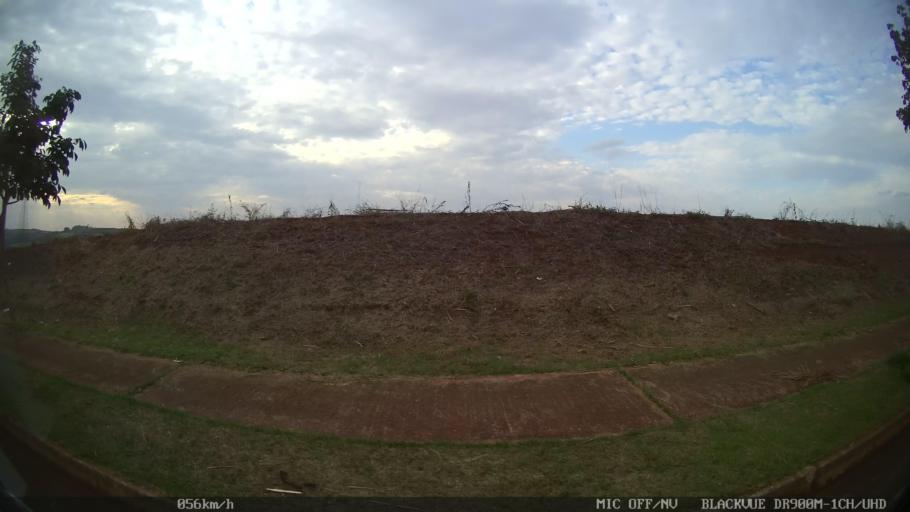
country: BR
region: Sao Paulo
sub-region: Americana
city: Americana
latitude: -22.6508
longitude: -47.3412
